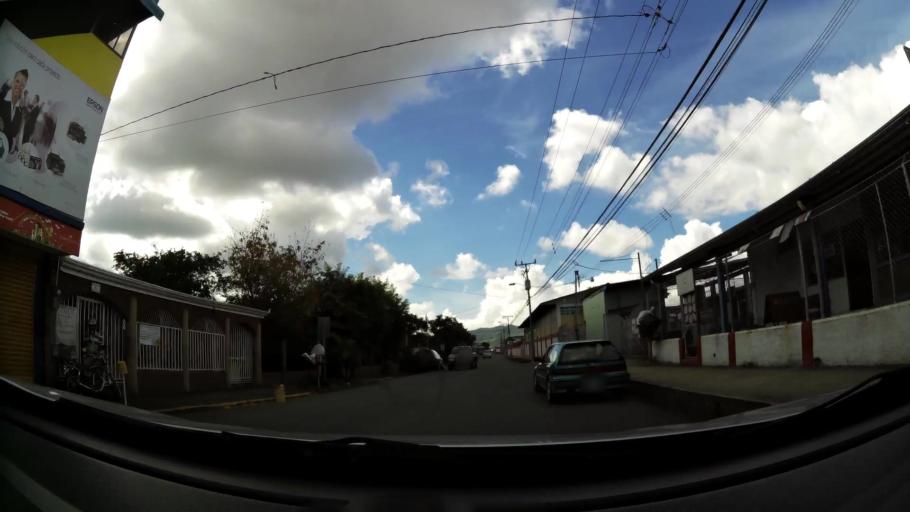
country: CR
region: San Jose
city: San Isidro
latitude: 9.3752
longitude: -83.7078
